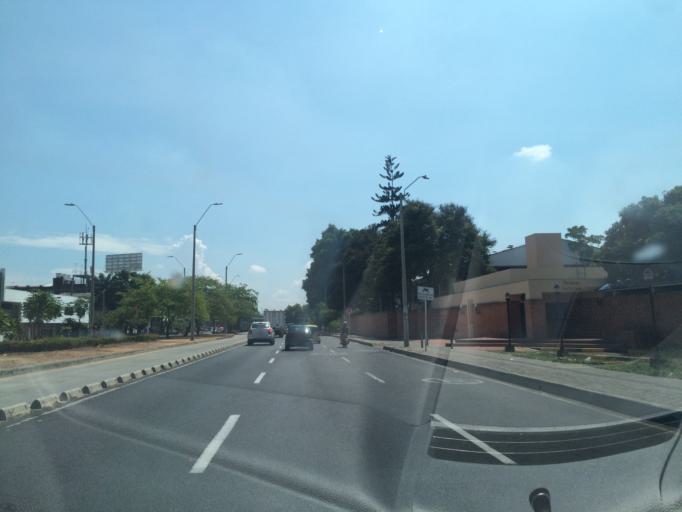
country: CO
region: Valle del Cauca
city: Cali
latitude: 3.4676
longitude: -76.5117
